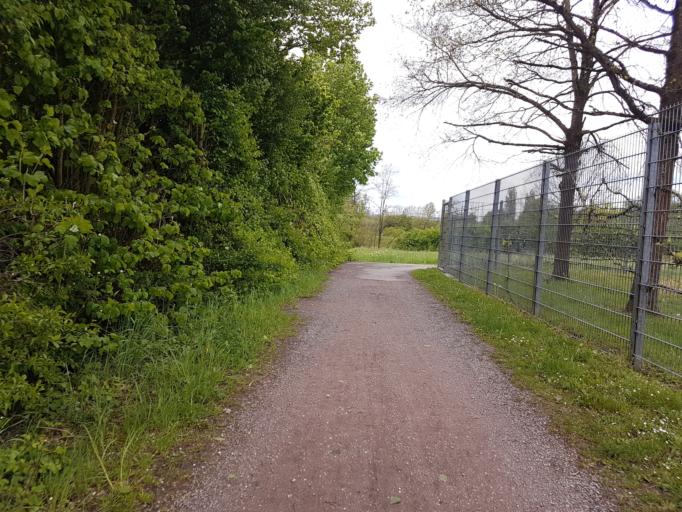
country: CH
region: Aargau
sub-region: Bezirk Zurzach
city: Koblenz
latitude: 47.6212
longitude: 8.2616
